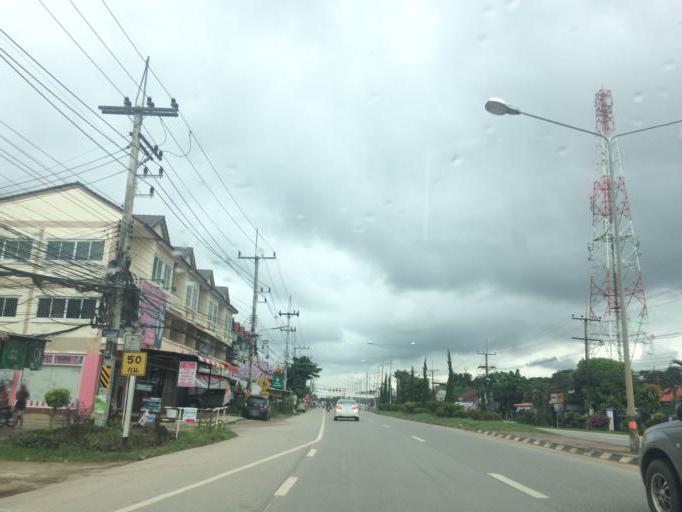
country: TH
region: Chiang Rai
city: Mae Chan
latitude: 20.0433
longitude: 99.8762
